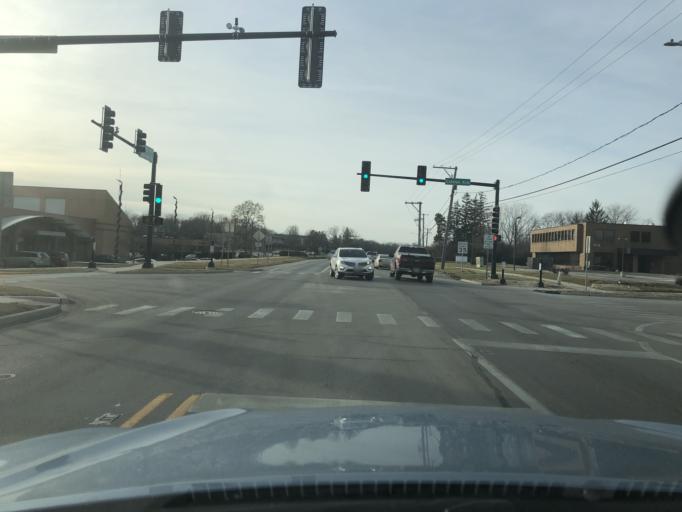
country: US
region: Illinois
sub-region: DuPage County
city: Itasca
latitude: 41.9715
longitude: -88.0195
